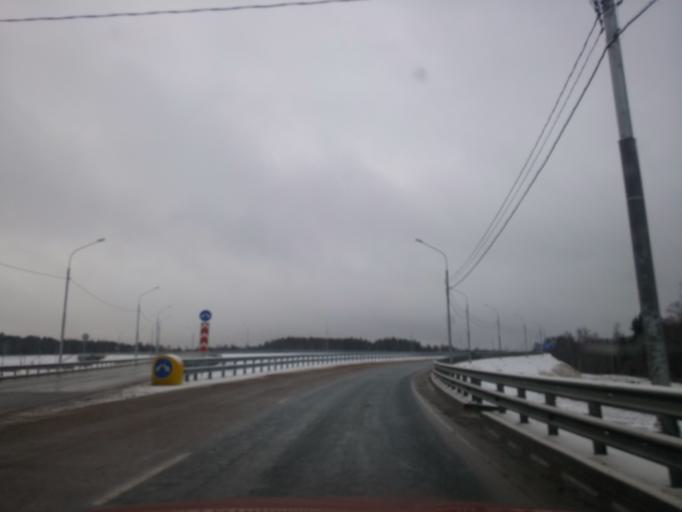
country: RU
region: Tverskaya
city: Likhoslavl'
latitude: 56.9477
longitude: 35.5034
